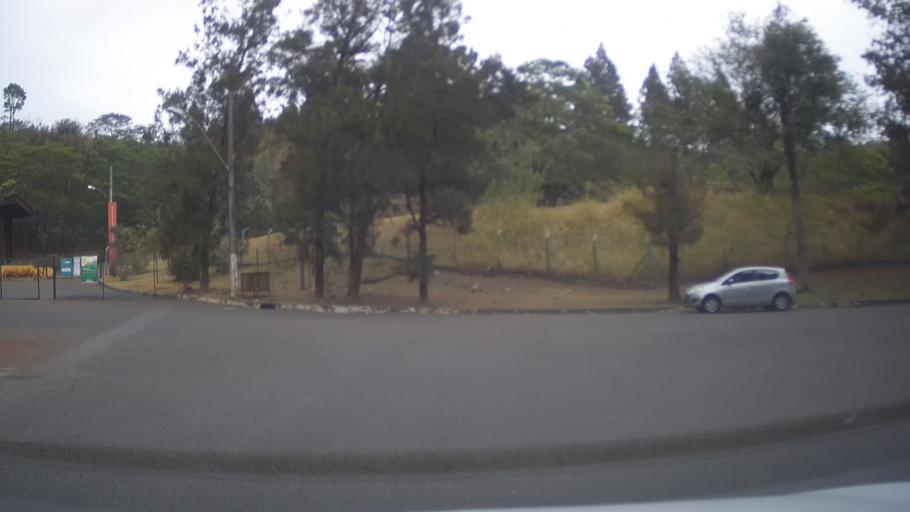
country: BR
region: Minas Gerais
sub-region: Belo Horizonte
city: Belo Horizonte
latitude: -19.9615
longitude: -43.9186
